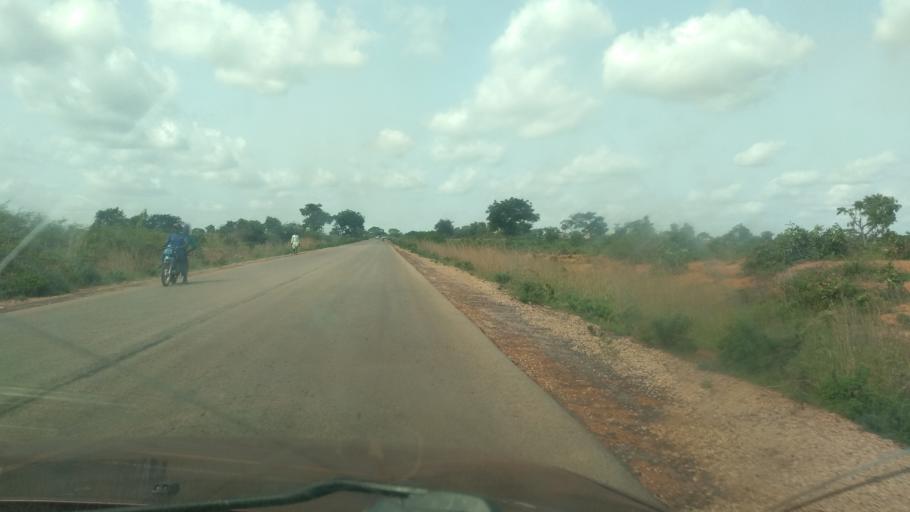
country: NG
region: Katsina
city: Sabuwa
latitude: 11.0513
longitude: 7.1606
